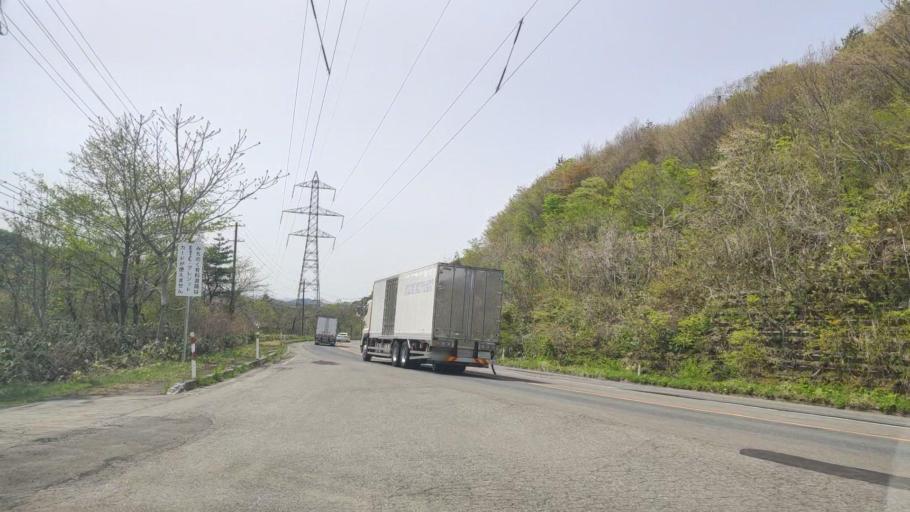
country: JP
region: Aomori
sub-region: Misawa Shi
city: Inuotose
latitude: 40.7907
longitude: 141.0990
